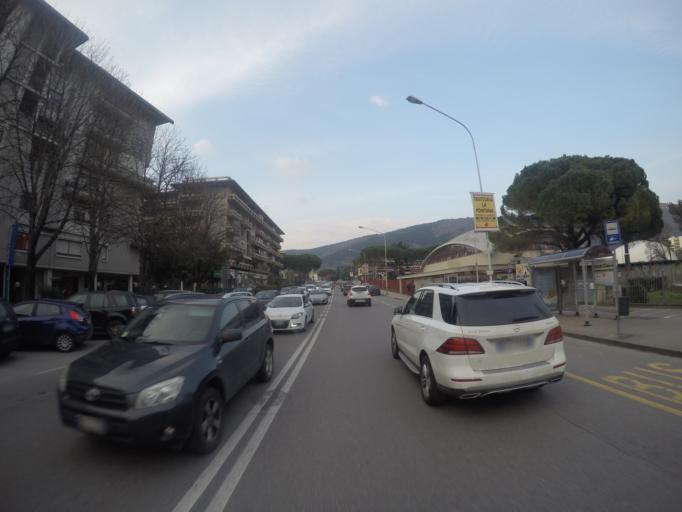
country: IT
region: Tuscany
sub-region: Provincia di Prato
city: Prato
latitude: 43.8687
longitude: 11.1141
